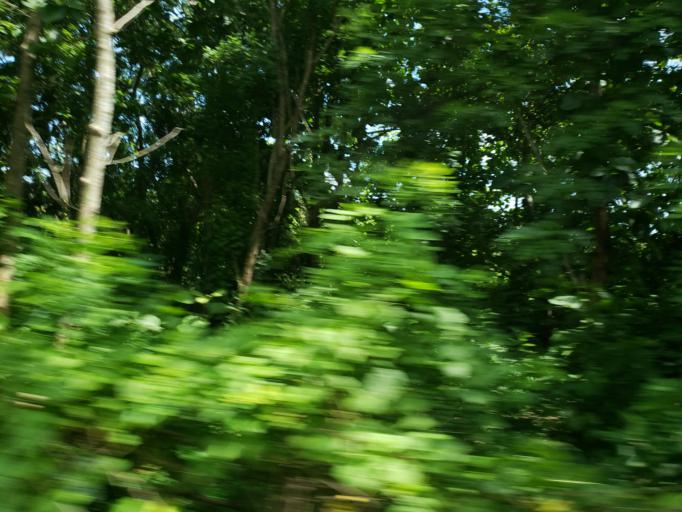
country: ID
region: Bali
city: Kangin
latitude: -8.8254
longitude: 115.1488
